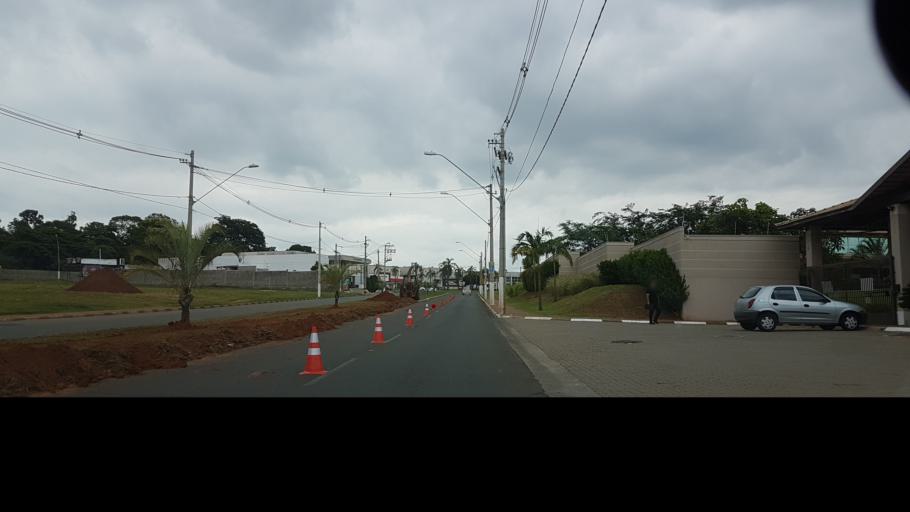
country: BR
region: Sao Paulo
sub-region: Paulinia
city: Paulinia
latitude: -22.7835
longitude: -47.1741
